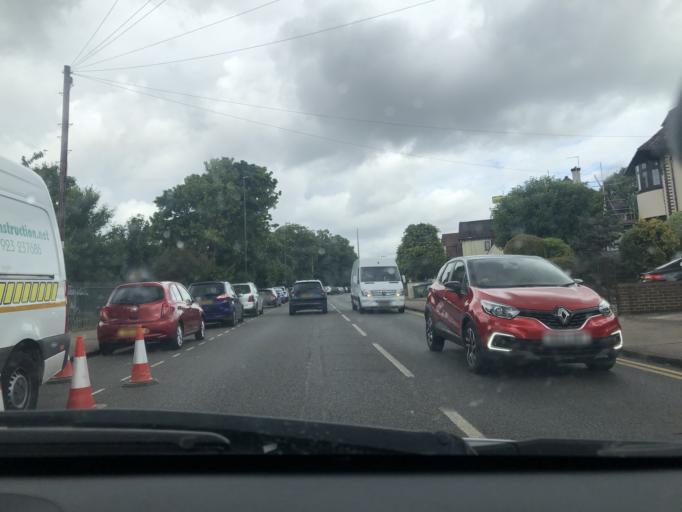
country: GB
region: England
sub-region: Greater London
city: Welling
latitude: 51.4536
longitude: 0.1229
